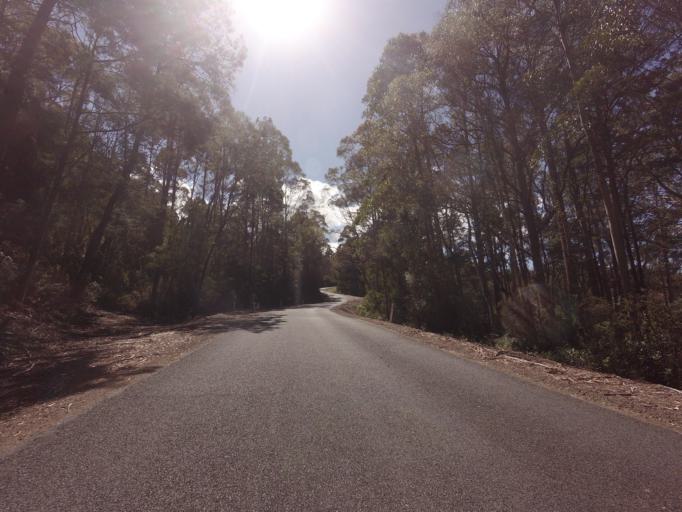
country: AU
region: Tasmania
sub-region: Break O'Day
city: St Helens
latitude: -41.6551
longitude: 148.2460
